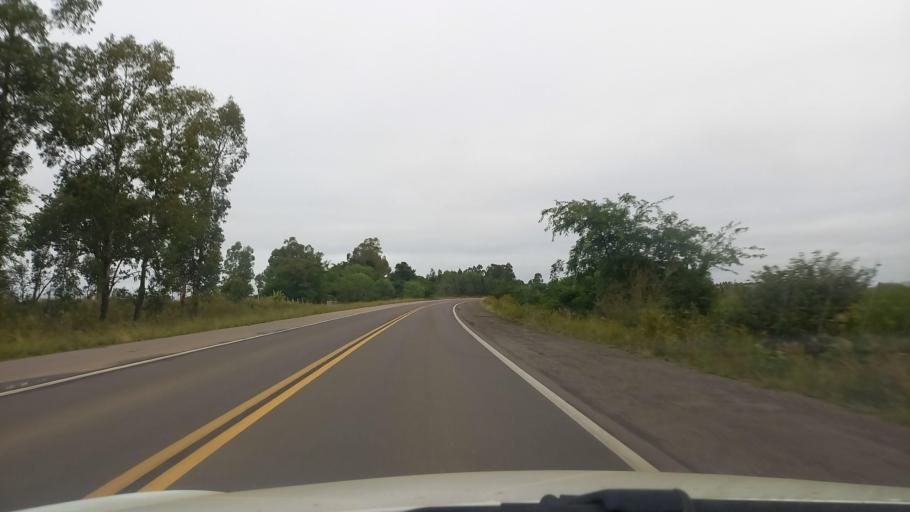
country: BR
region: Rio Grande do Sul
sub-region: Sao Pedro Do Sul
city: Sao Pedro do Sul
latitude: -29.7969
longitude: -54.1198
